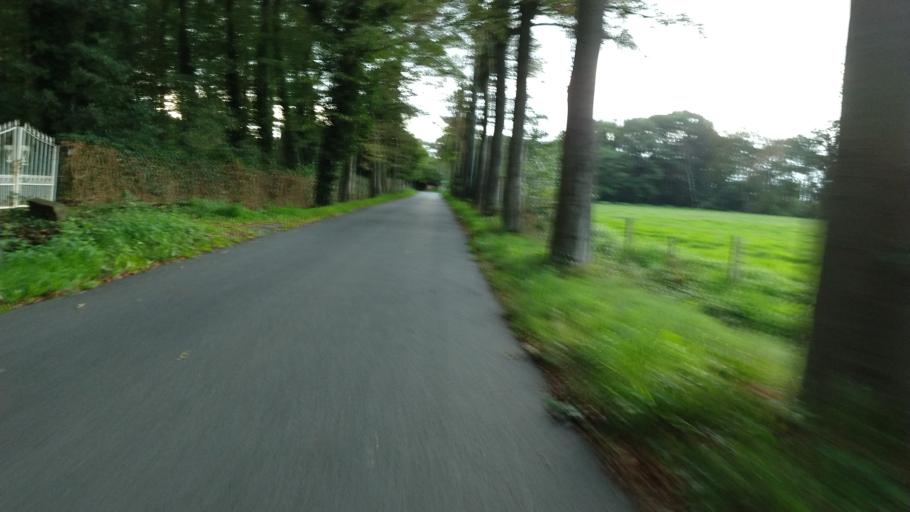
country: BE
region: Flanders
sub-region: Provincie Oost-Vlaanderen
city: Aalter
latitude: 51.0793
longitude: 3.4813
